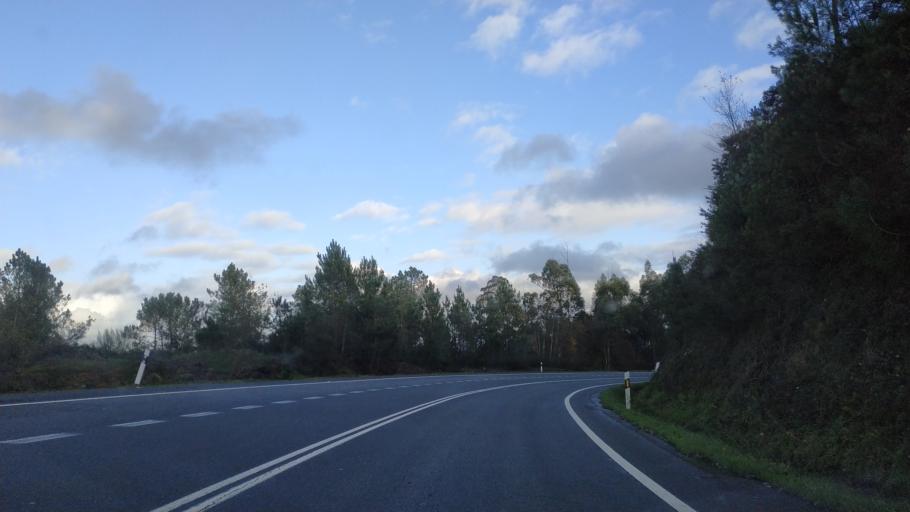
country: ES
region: Galicia
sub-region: Provincia de Pontevedra
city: Silleda
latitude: 42.7985
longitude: -8.1791
